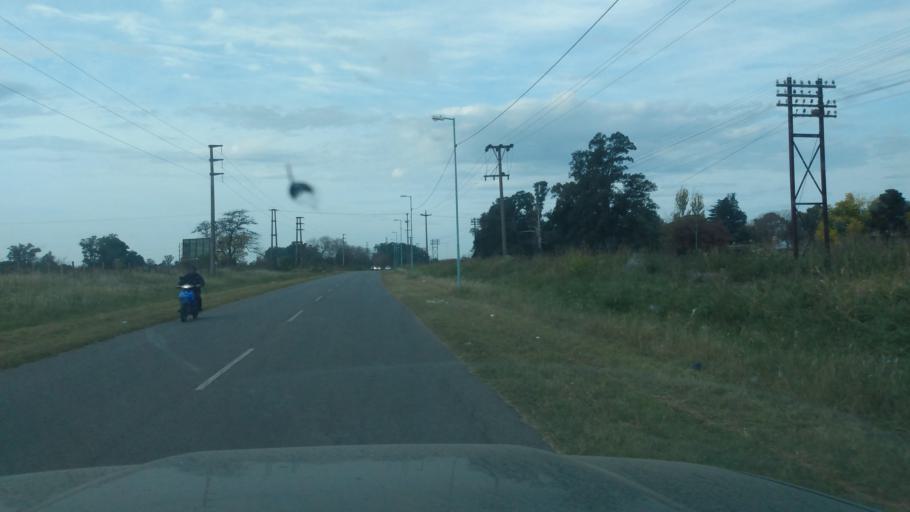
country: AR
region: Buenos Aires
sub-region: Partido de Lujan
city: Lujan
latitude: -34.5925
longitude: -59.1476
